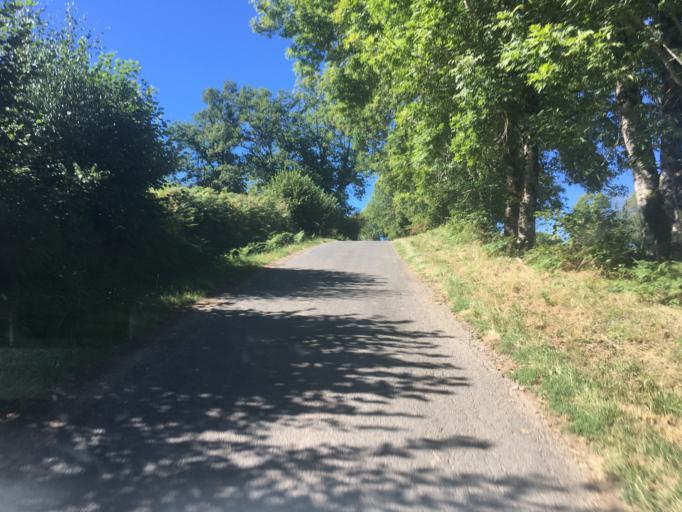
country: FR
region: Limousin
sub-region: Departement de la Correze
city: Bort-les-Orgues
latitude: 45.4010
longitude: 2.4801
